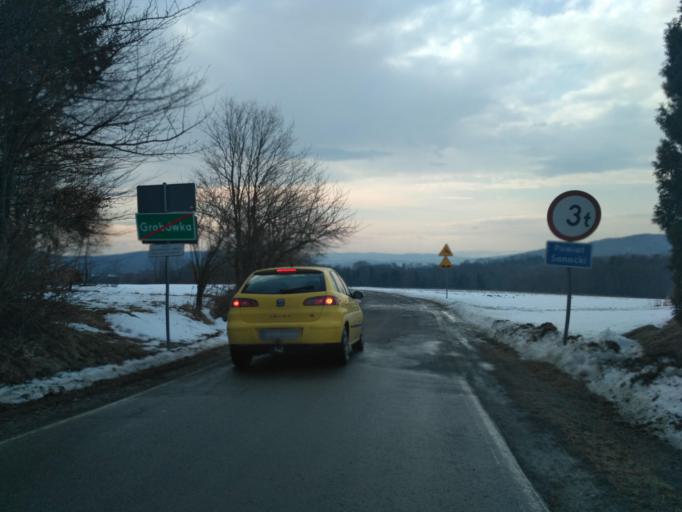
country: PL
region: Subcarpathian Voivodeship
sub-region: Powiat brzozowski
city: Dydnia
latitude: 49.6470
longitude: 22.1600
